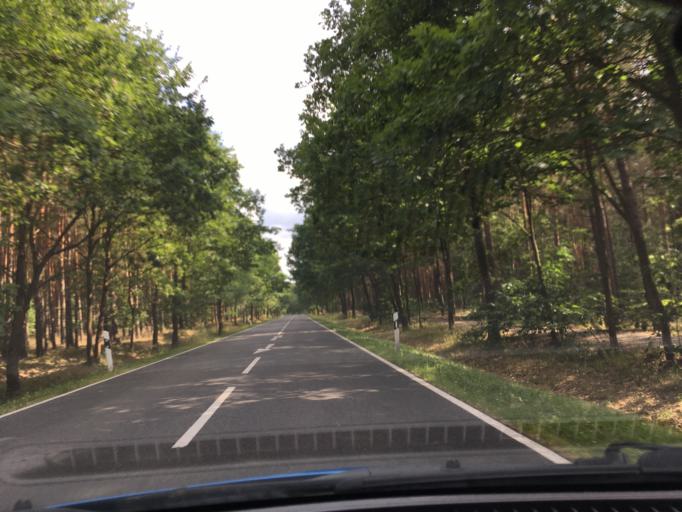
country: DE
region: Mecklenburg-Vorpommern
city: Lubtheen
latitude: 53.2870
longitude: 11.0931
